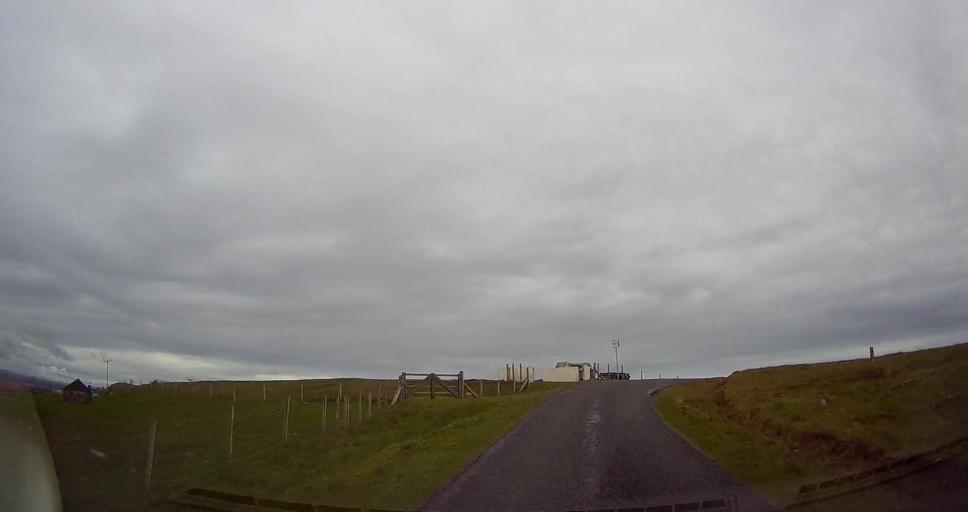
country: GB
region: Scotland
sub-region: Shetland Islands
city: Lerwick
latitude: 60.4813
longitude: -1.6091
